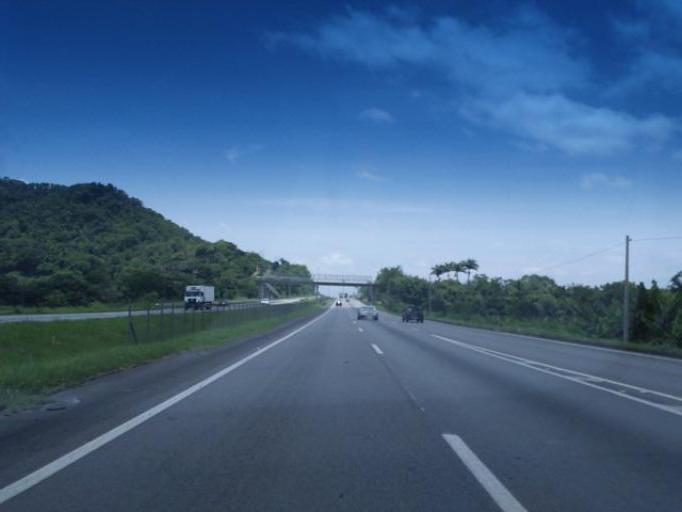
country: BR
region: Sao Paulo
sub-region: Miracatu
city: Miracatu
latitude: -24.3144
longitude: -47.5216
